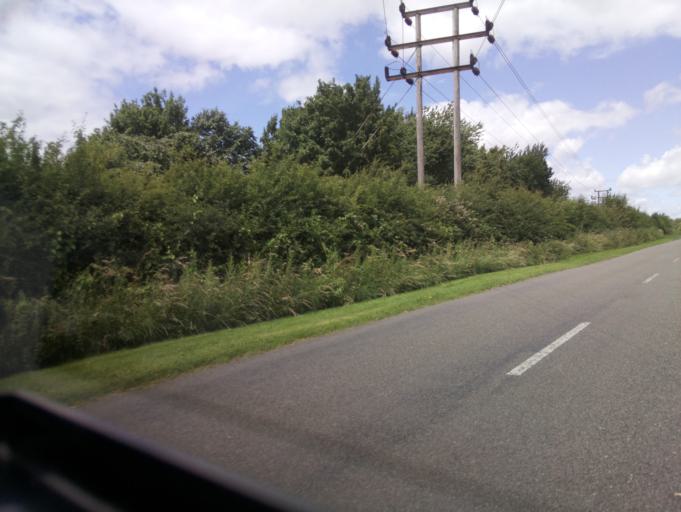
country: GB
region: England
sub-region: Nottinghamshire
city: Cotgrave
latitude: 52.8583
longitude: -1.0701
